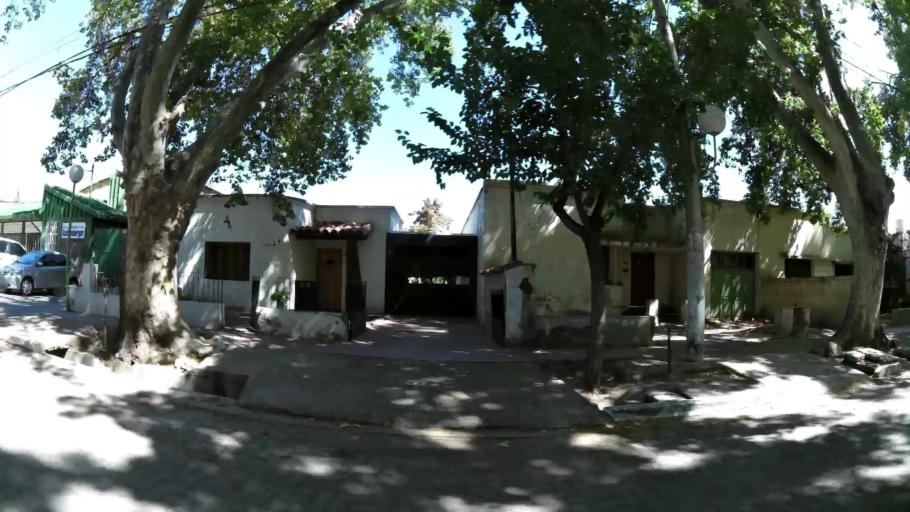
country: AR
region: Mendoza
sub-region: Departamento de Godoy Cruz
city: Godoy Cruz
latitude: -32.9613
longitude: -68.8531
